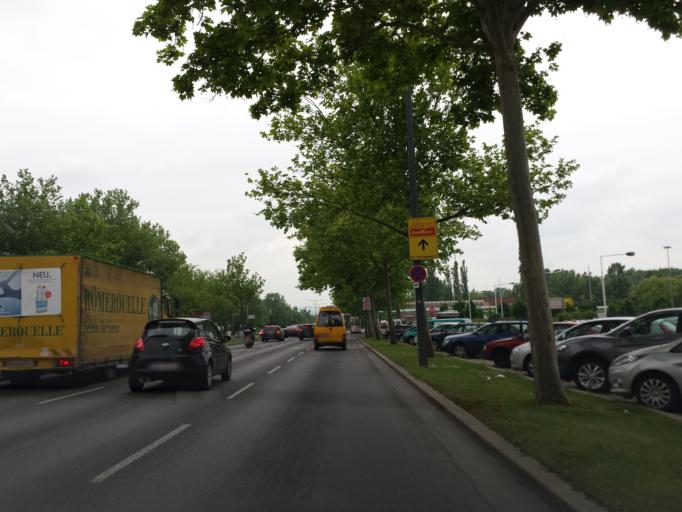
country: AT
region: Lower Austria
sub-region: Politischer Bezirk Modling
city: Vosendorf
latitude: 48.1673
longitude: 16.3483
